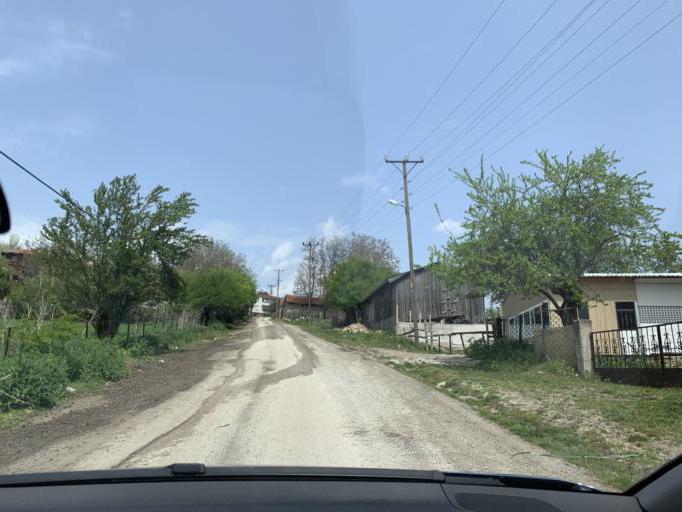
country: TR
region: Bolu
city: Bolu
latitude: 40.7649
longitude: 31.7072
